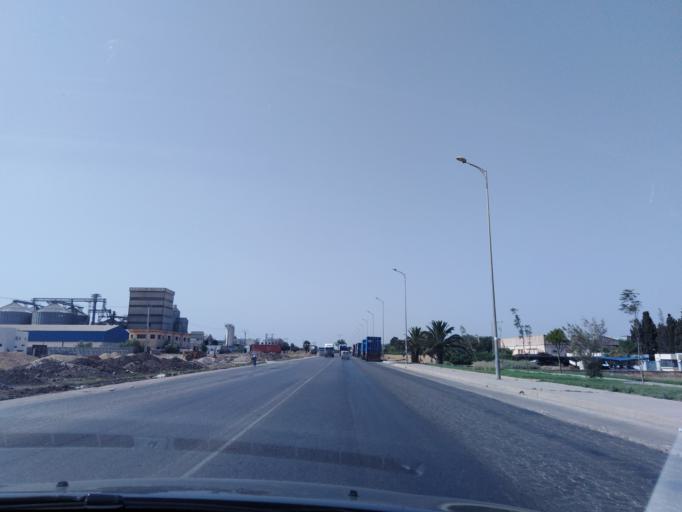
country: MA
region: Chaouia-Ouardigha
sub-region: Settat Province
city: Berrechid
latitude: 33.2419
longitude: -7.5870
